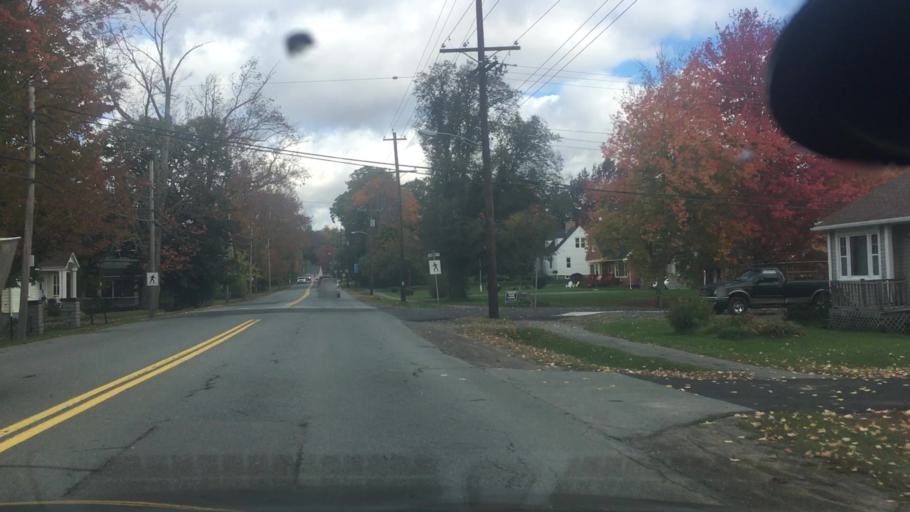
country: CA
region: Nova Scotia
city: Windsor
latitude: 44.9818
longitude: -64.1301
